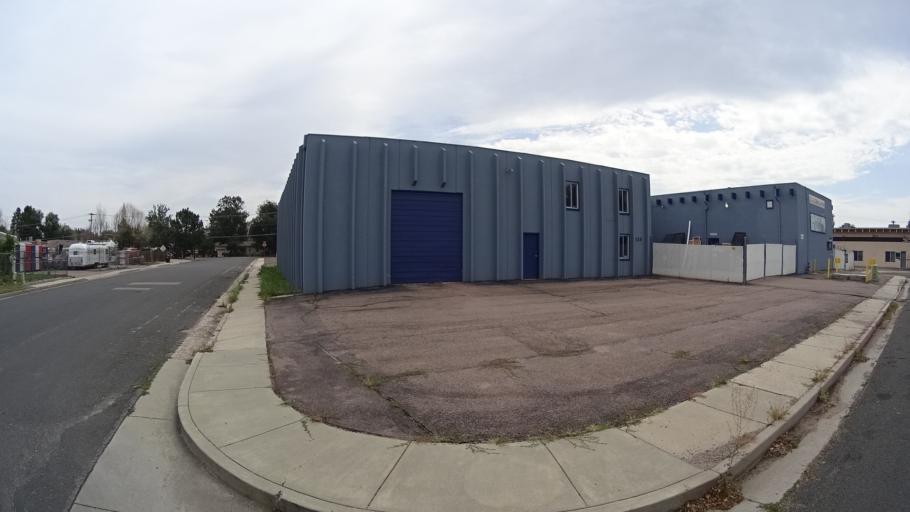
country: US
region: Colorado
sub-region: El Paso County
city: Colorado Springs
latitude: 38.8773
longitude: -104.8281
